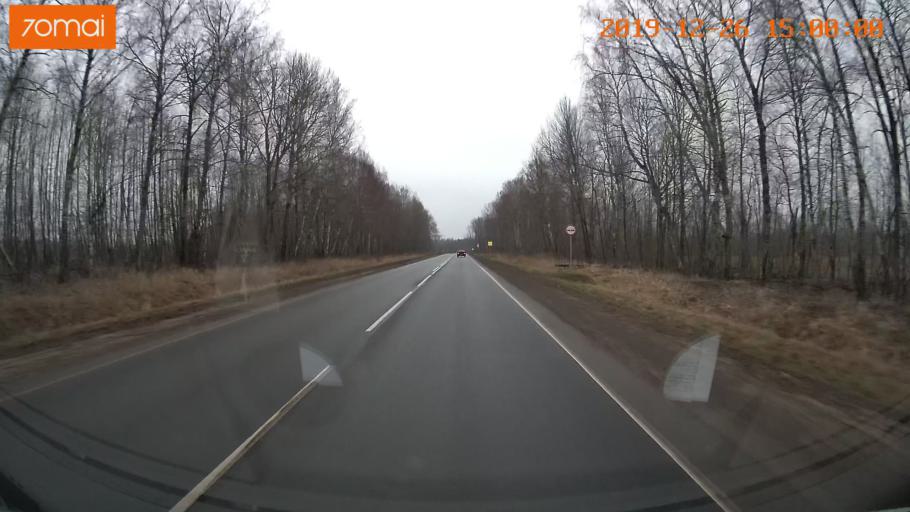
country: RU
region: Jaroslavl
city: Rybinsk
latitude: 58.2512
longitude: 38.8491
